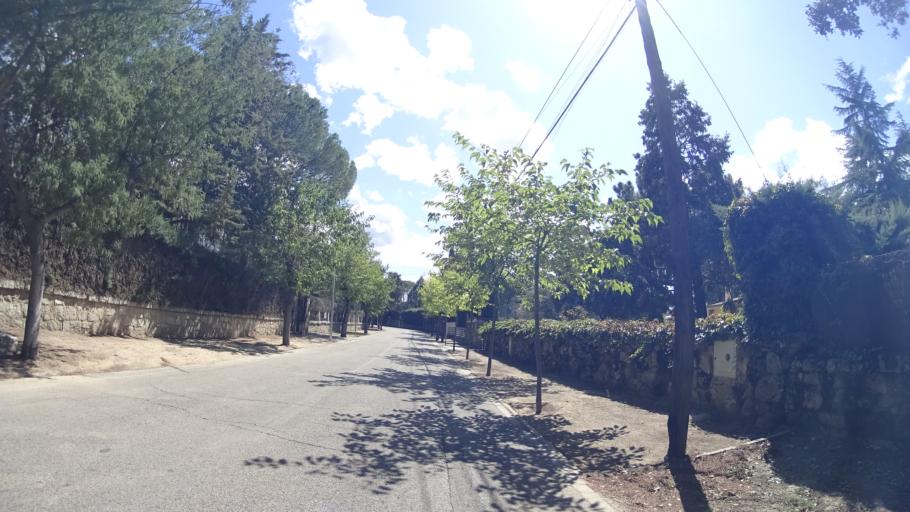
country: ES
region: Madrid
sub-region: Provincia de Madrid
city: Torrelodones
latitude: 40.5699
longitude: -3.9514
